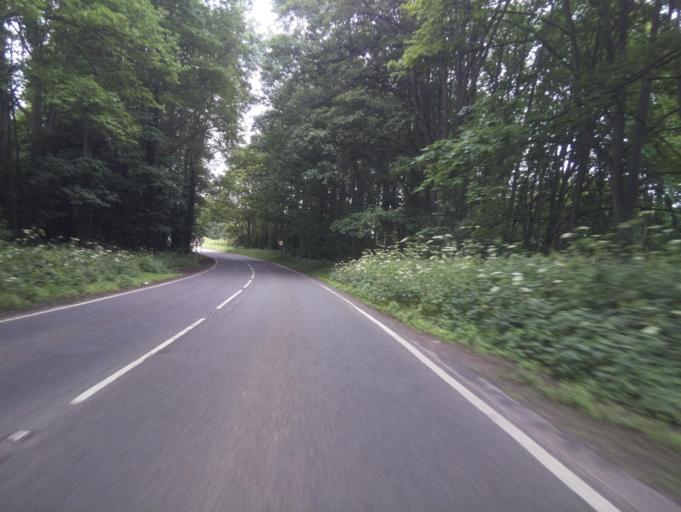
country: GB
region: England
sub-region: District of Rutland
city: Edith Weston
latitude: 52.6437
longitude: -0.6228
